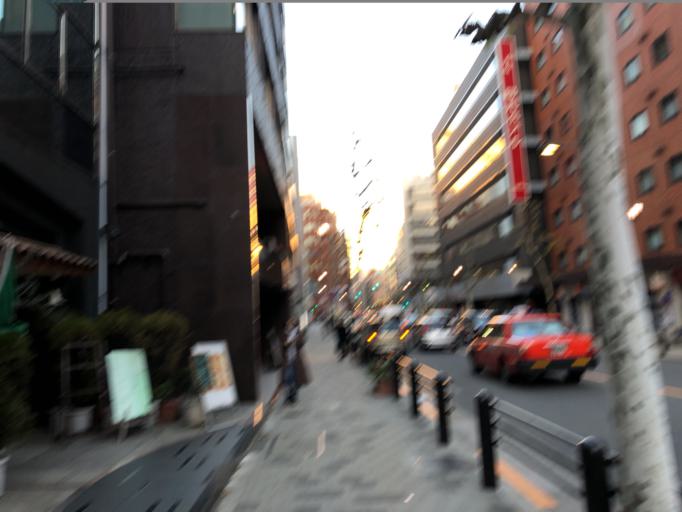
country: JP
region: Tokyo
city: Tokyo
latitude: 35.6695
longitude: 139.7328
